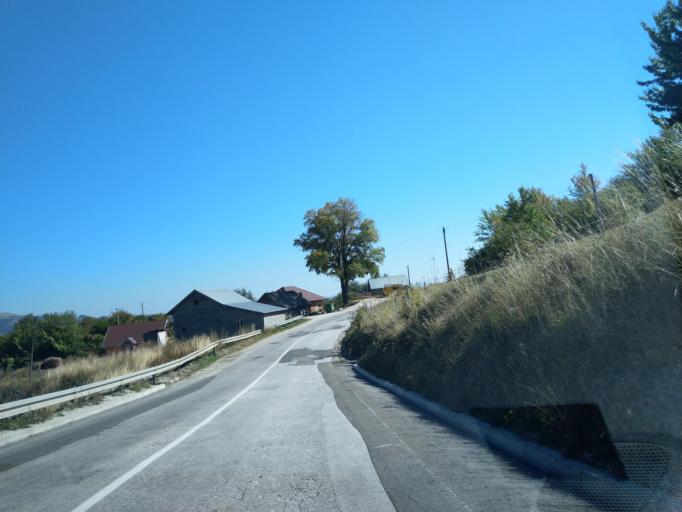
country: RS
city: Sokolovica
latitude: 43.2614
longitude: 20.2324
